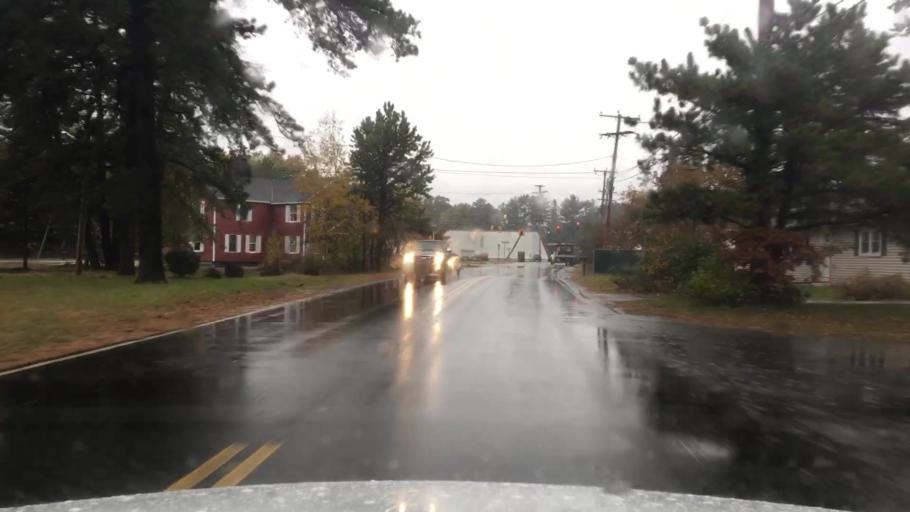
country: US
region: New Hampshire
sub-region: Strafford County
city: Rochester
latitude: 43.3455
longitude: -70.9732
